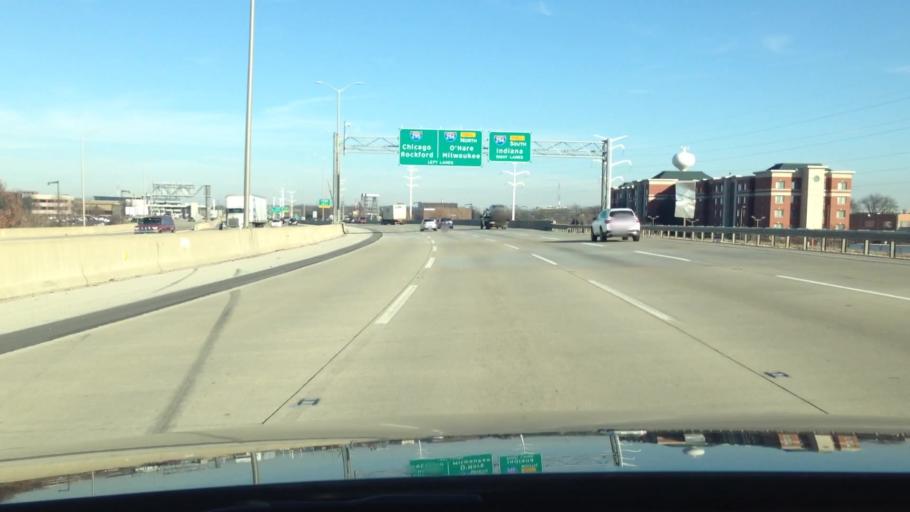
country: US
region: Illinois
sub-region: DuPage County
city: Oakbrook Terrace
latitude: 41.8454
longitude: -87.9455
